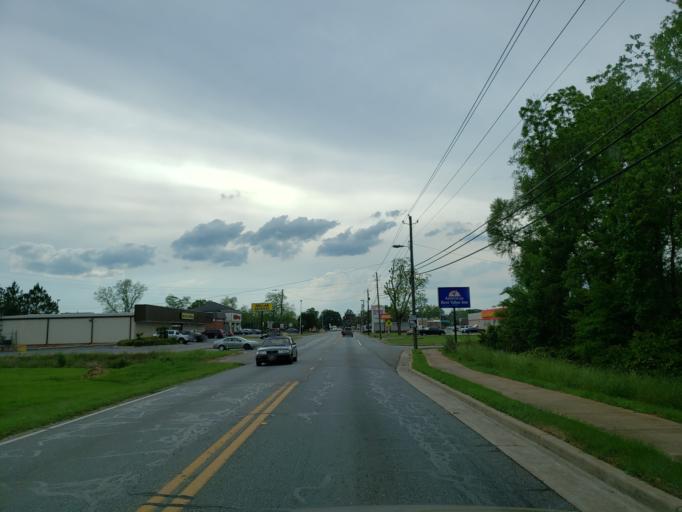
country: US
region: Georgia
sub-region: Macon County
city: Montezuma
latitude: 32.2935
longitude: -84.0164
